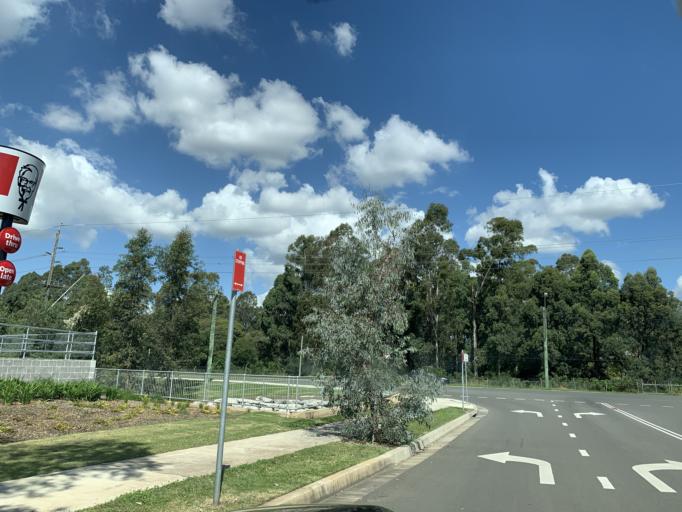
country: AU
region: New South Wales
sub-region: Penrith Municipality
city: Penrith
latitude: -33.7307
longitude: 150.7026
